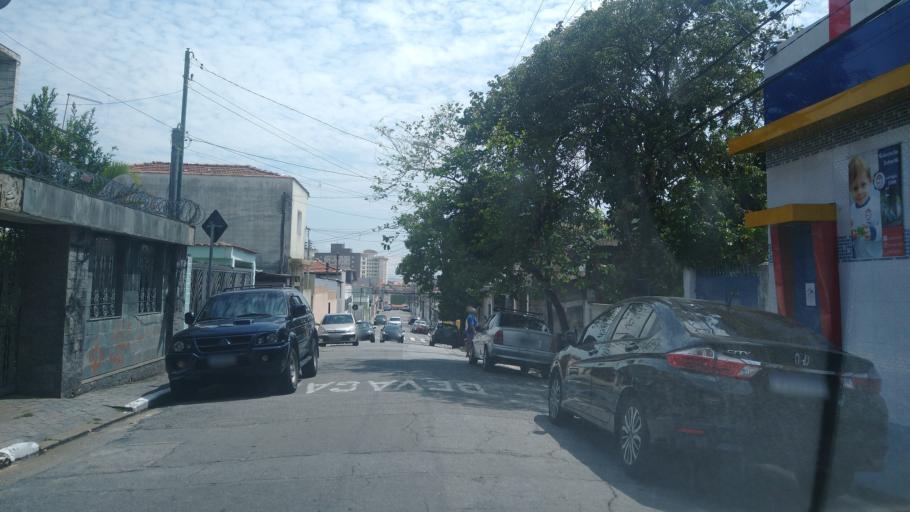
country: BR
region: Sao Paulo
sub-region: Sao Paulo
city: Sao Paulo
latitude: -23.4942
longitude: -46.5963
